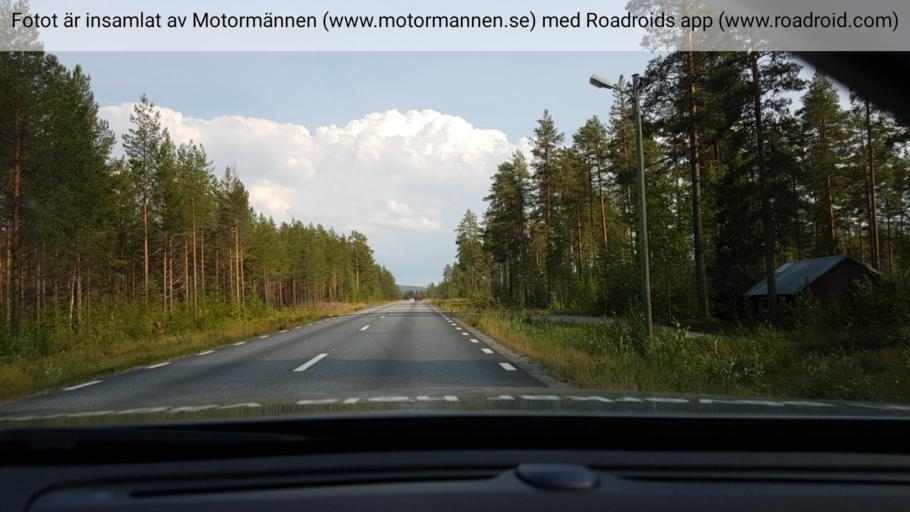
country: SE
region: Vaesterbotten
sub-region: Bjurholms Kommun
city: Bjurholm
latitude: 64.2876
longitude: 19.2022
